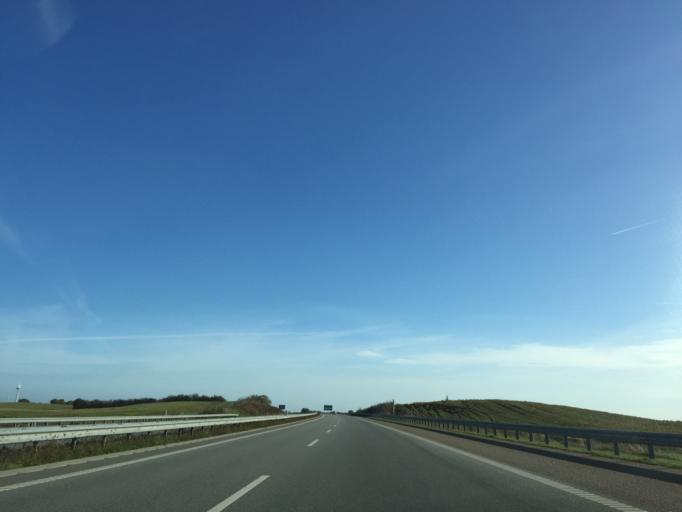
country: DK
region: South Denmark
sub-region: Aabenraa Kommune
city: Aabenraa
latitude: 54.9450
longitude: 9.4606
